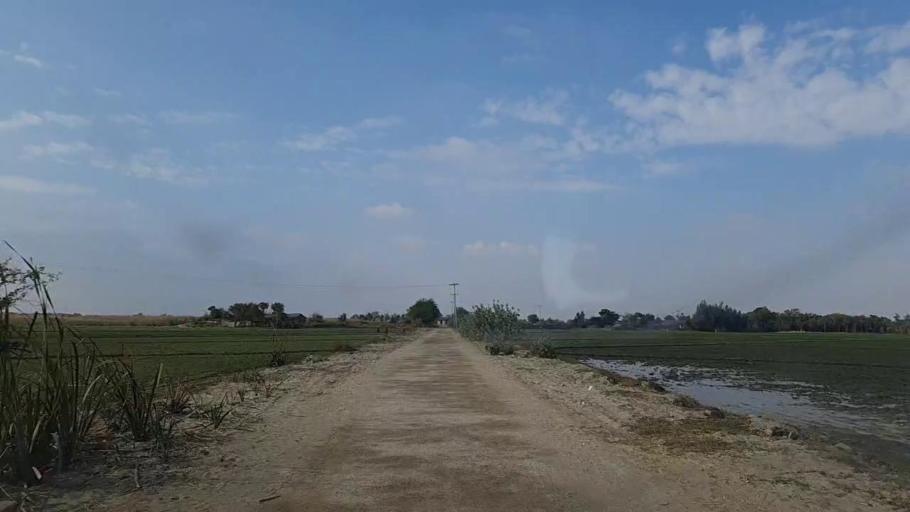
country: PK
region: Sindh
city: Sanghar
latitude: 26.2735
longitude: 69.0110
